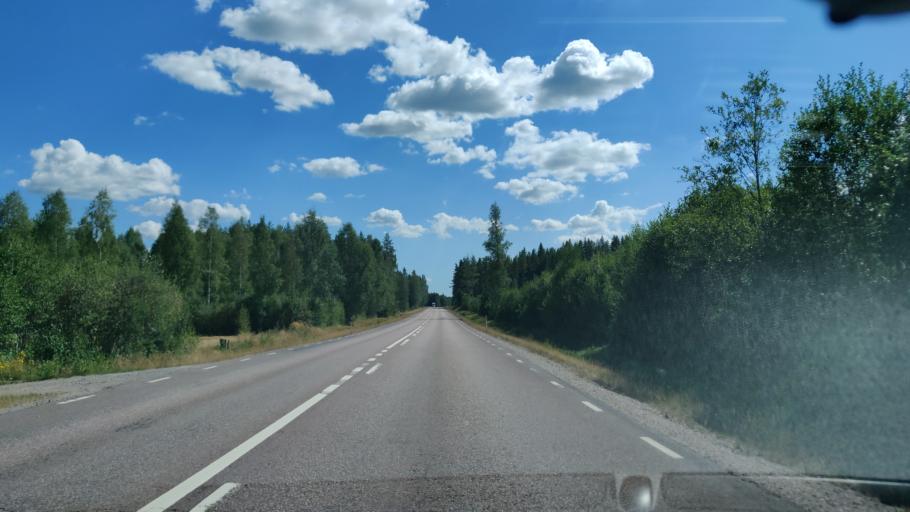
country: SE
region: Vaermland
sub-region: Hagfors Kommun
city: Ekshaerad
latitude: 60.2108
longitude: 13.4856
